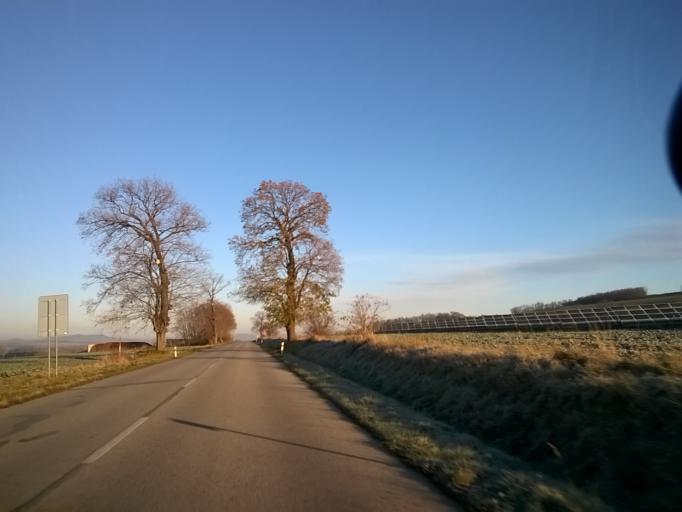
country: SK
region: Nitriansky
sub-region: Okres Nitra
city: Nitra
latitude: 48.4064
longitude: 18.1177
